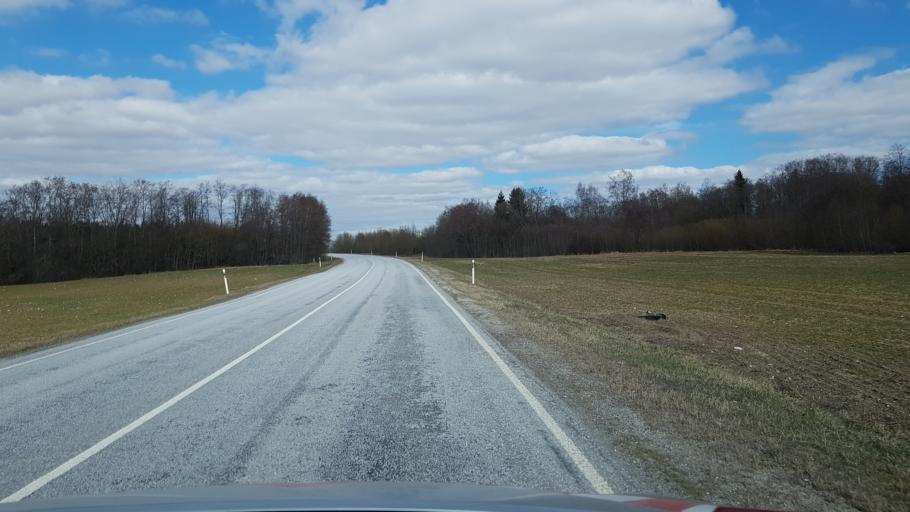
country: EE
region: Laeaene-Virumaa
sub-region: Rakke vald
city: Rakke
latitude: 58.9555
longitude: 26.2764
